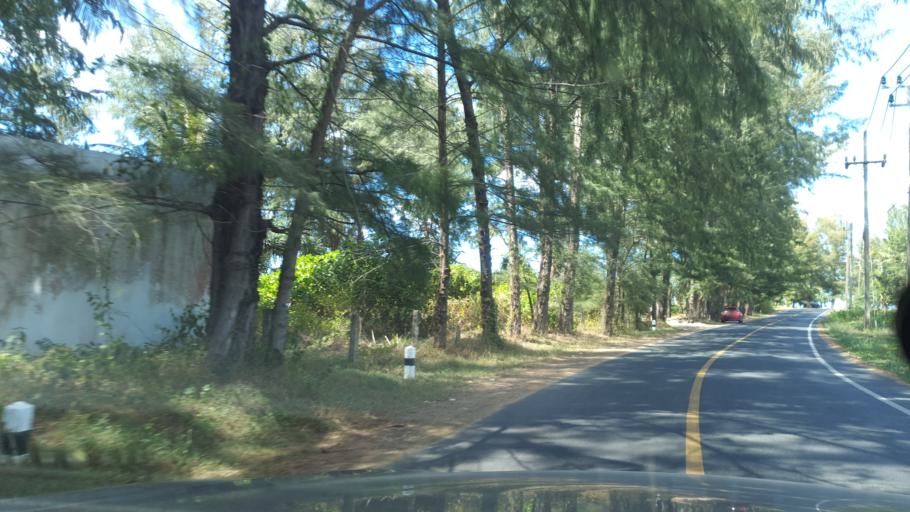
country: TH
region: Phangnga
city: Thai Mueang
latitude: 8.2939
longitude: 98.2728
